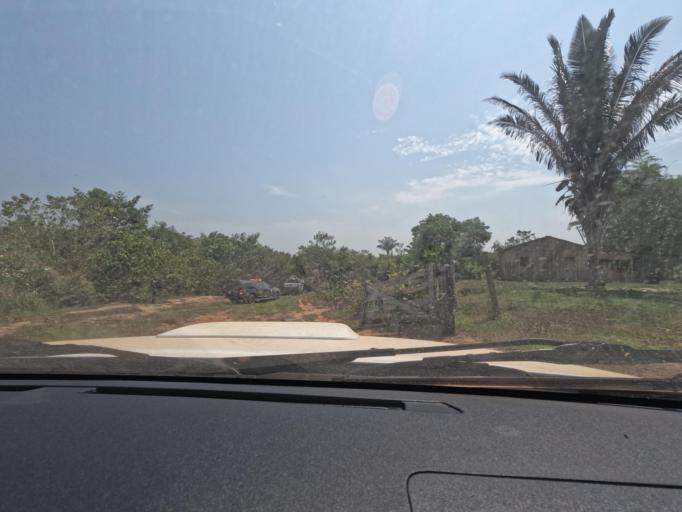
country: BR
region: Rondonia
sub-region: Porto Velho
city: Porto Velho
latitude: -8.6680
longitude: -64.2666
